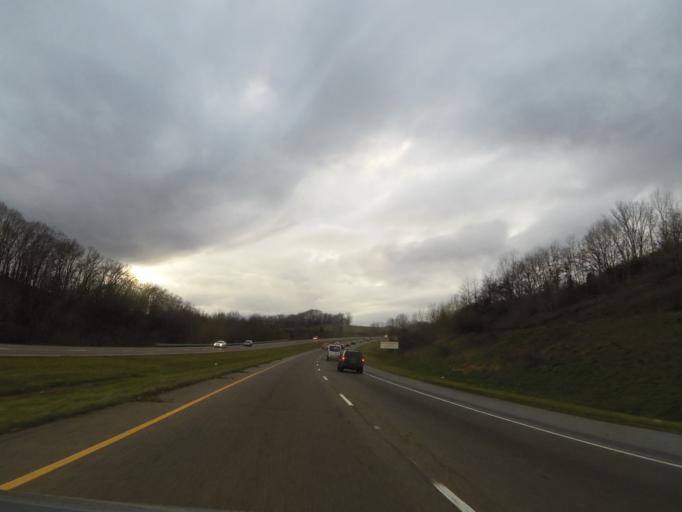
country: US
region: Tennessee
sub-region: Carter County
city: Central
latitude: 36.3172
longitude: -82.2894
